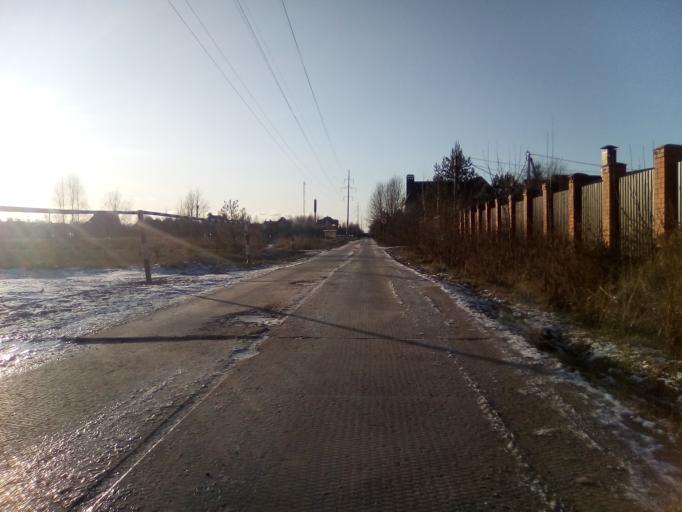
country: RU
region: Moskovskaya
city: Kokoshkino
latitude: 55.6487
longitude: 37.1566
